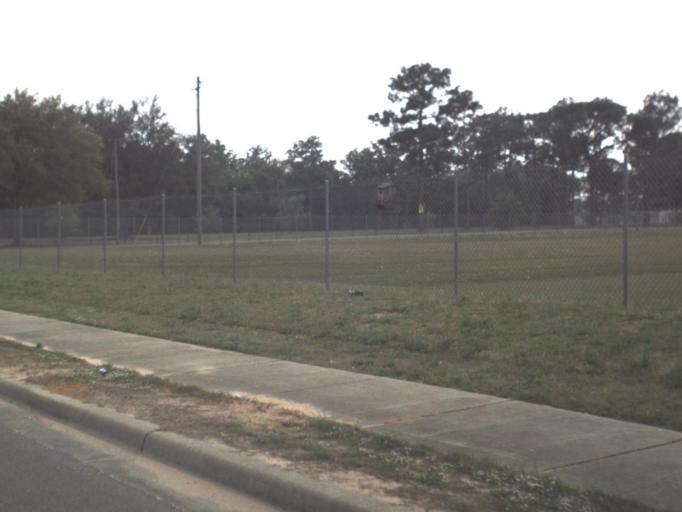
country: US
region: Florida
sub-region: Santa Rosa County
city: Milton
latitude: 30.6432
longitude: -87.0555
